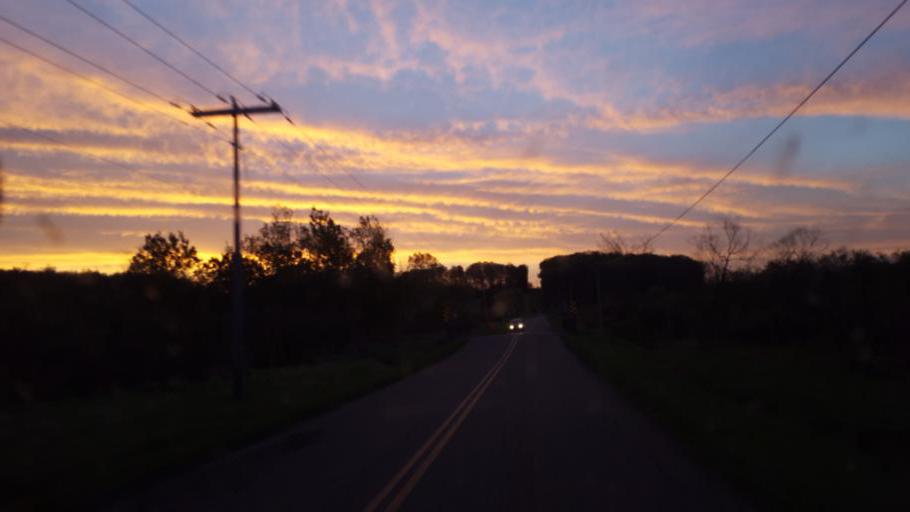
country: US
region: Ohio
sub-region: Knox County
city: Fredericktown
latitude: 40.4737
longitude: -82.4610
